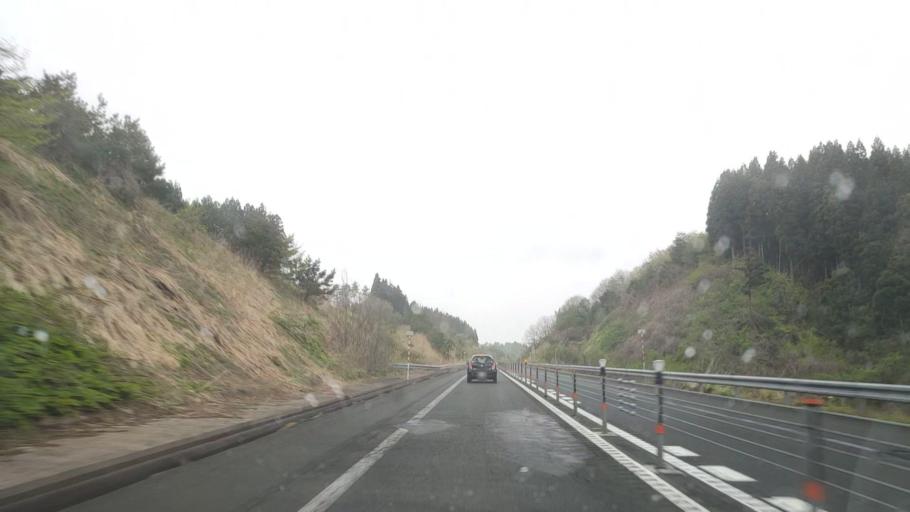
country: JP
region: Akita
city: Noshiromachi
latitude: 40.2050
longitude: 140.1621
